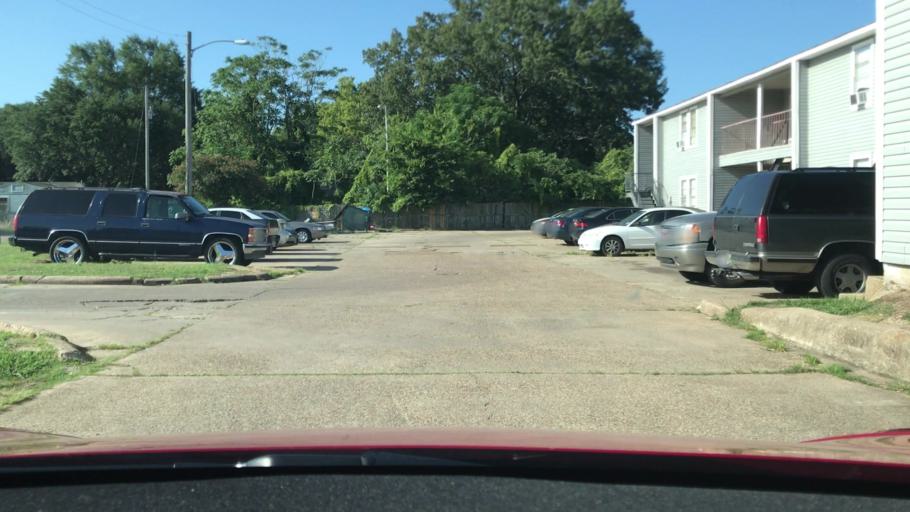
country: US
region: Louisiana
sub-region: Bossier Parish
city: Bossier City
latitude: 32.4390
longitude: -93.7655
